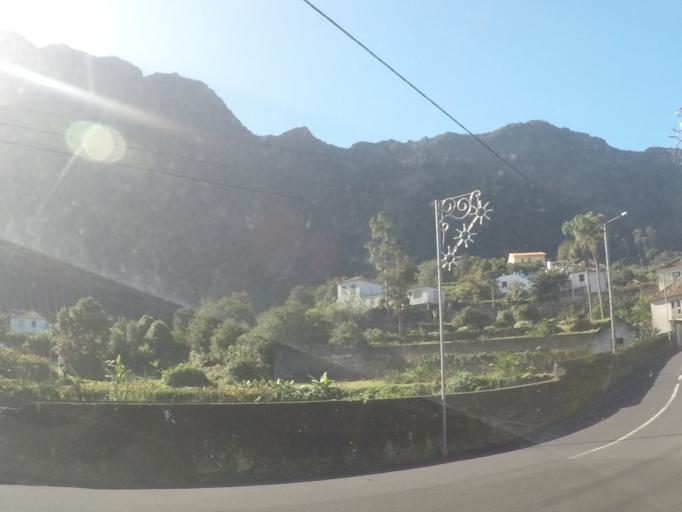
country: PT
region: Madeira
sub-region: Santana
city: Santana
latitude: 32.8271
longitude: -16.9543
